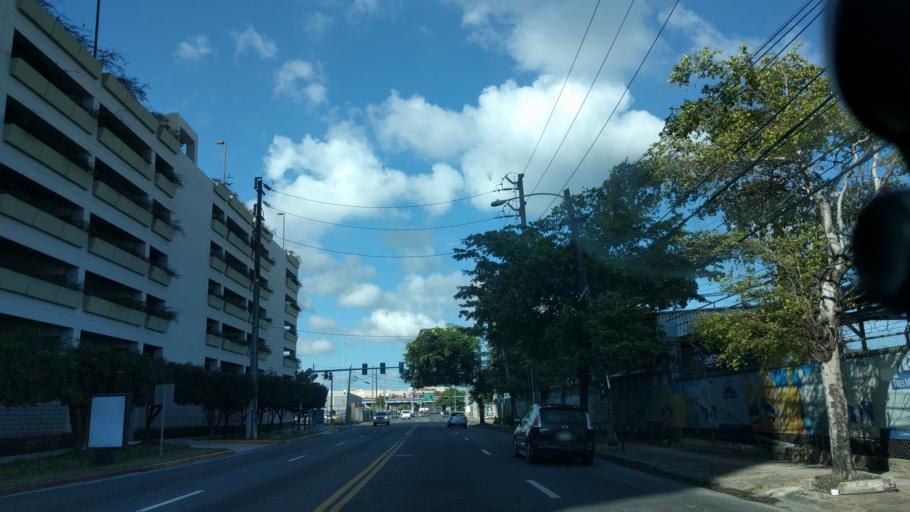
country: PR
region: Catano
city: Catano
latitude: 18.4237
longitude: -66.0681
